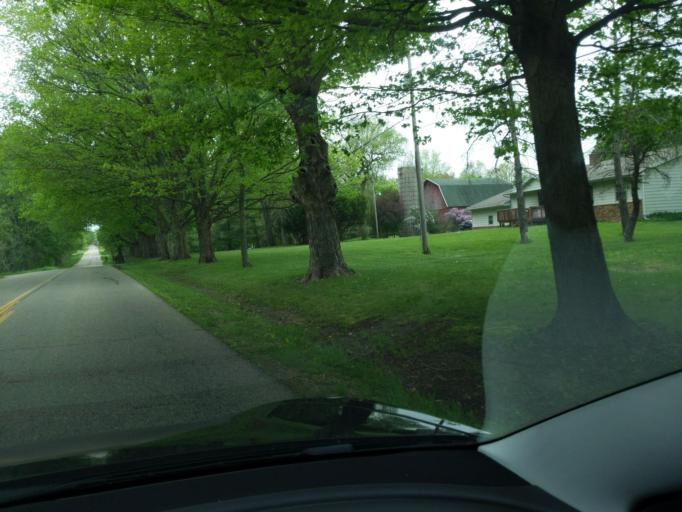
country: US
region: Michigan
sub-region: Ingham County
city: Holt
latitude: 42.5578
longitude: -84.5424
